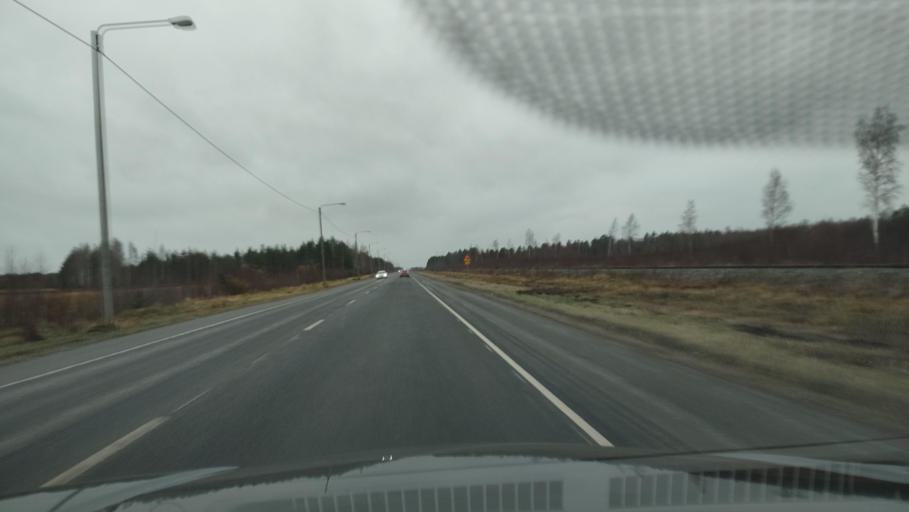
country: FI
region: Southern Ostrobothnia
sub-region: Seinaejoki
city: Ilmajoki
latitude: 62.7529
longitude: 22.6519
